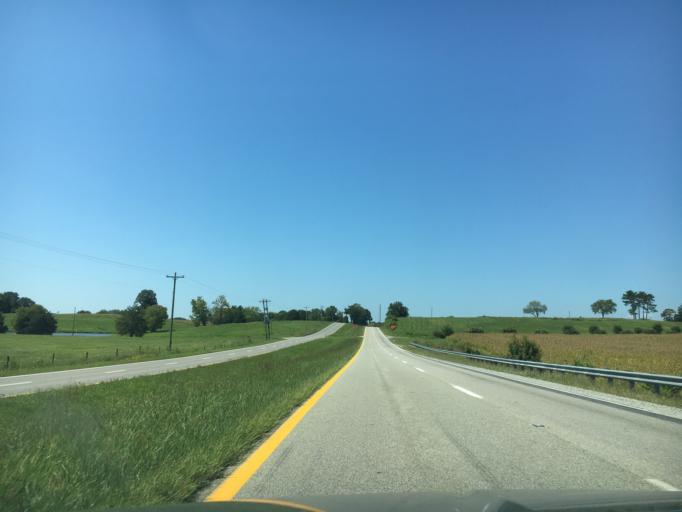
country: US
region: Virginia
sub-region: City of Danville
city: Danville
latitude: 36.5813
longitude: -79.1731
